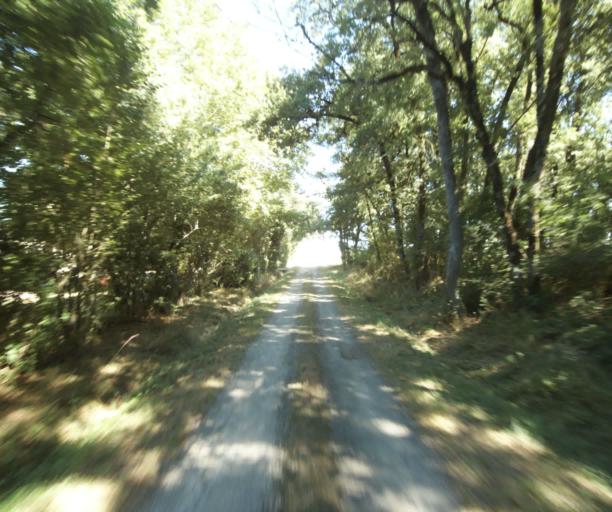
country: FR
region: Midi-Pyrenees
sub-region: Departement de la Haute-Garonne
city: Saint-Felix-Lauragais
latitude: 43.5106
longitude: 1.9003
